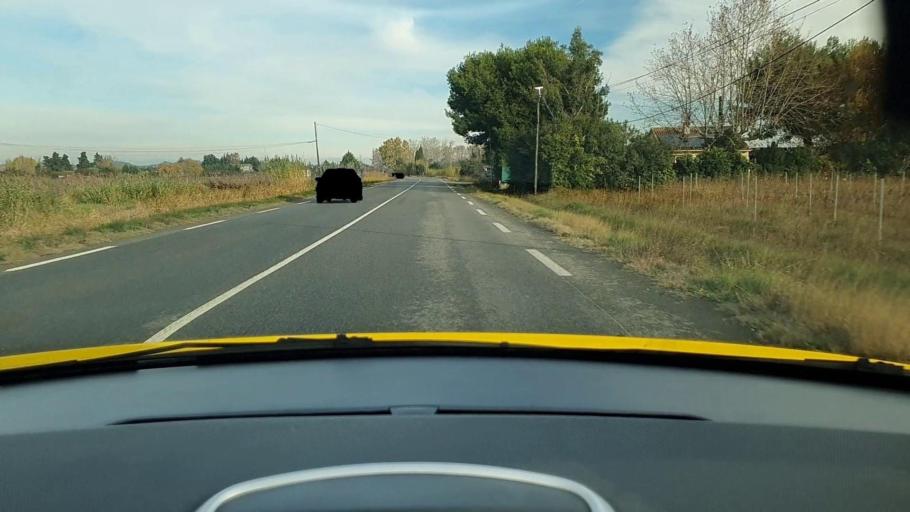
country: FR
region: Languedoc-Roussillon
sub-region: Departement du Gard
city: Beaucaire
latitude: 43.7719
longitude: 4.6209
